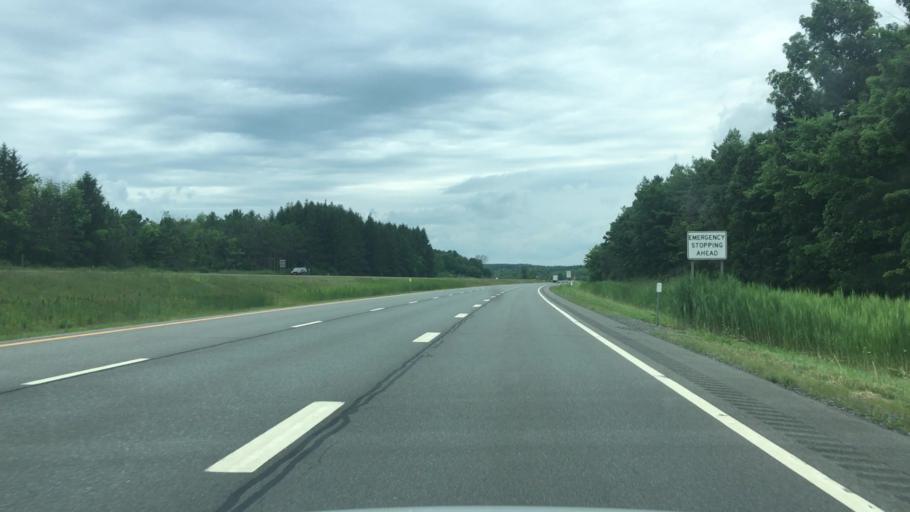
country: US
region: New York
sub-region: Schoharie County
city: Schoharie
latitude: 42.7242
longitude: -74.2281
